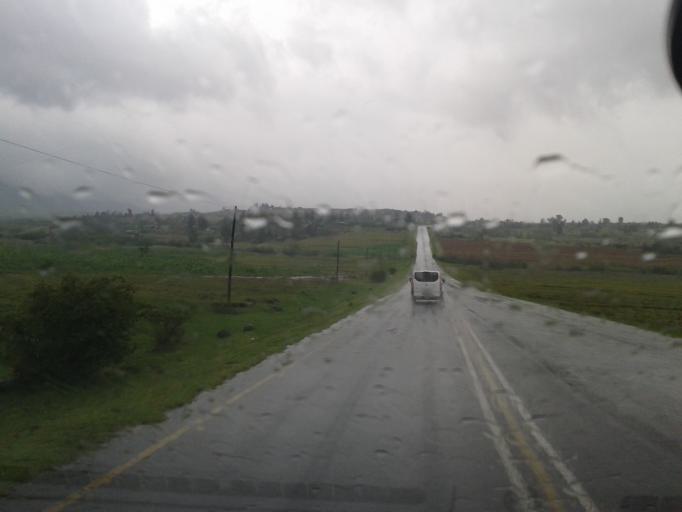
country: LS
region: Maseru
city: Nako
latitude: -29.6346
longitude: 27.4802
